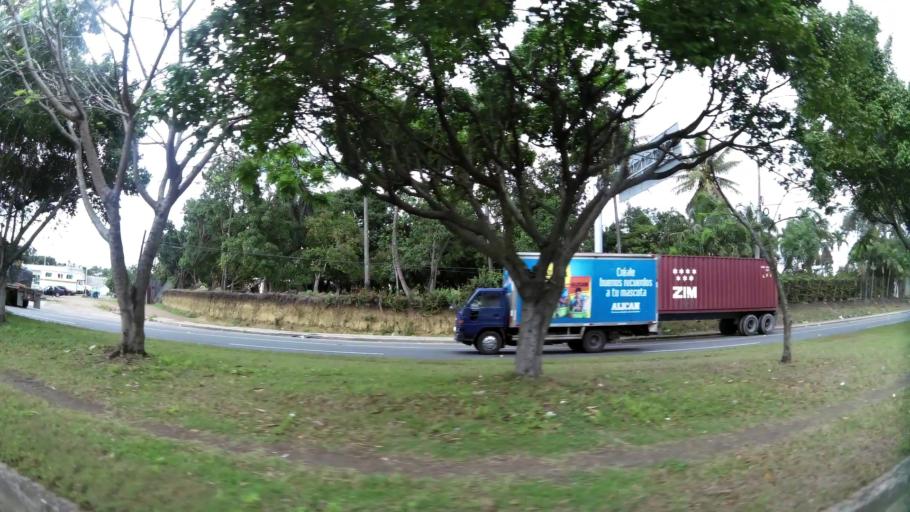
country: DO
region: Santiago
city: Licey al Medio
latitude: 19.4116
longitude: -70.6412
